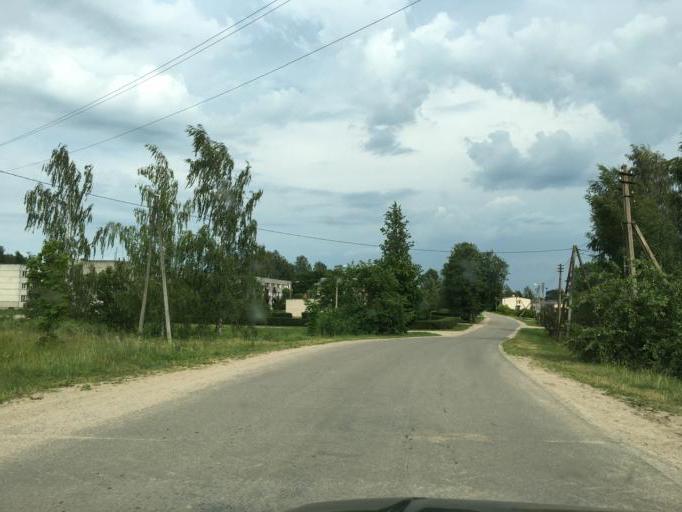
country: LV
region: Vilanu
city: Vilani
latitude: 56.6811
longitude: 26.9380
